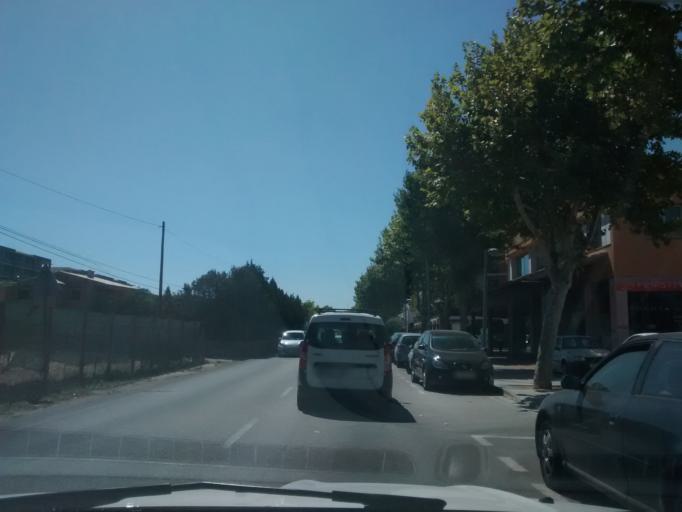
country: ES
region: Balearic Islands
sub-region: Illes Balears
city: Port d'Alcudia
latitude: 39.8448
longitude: 3.1323
